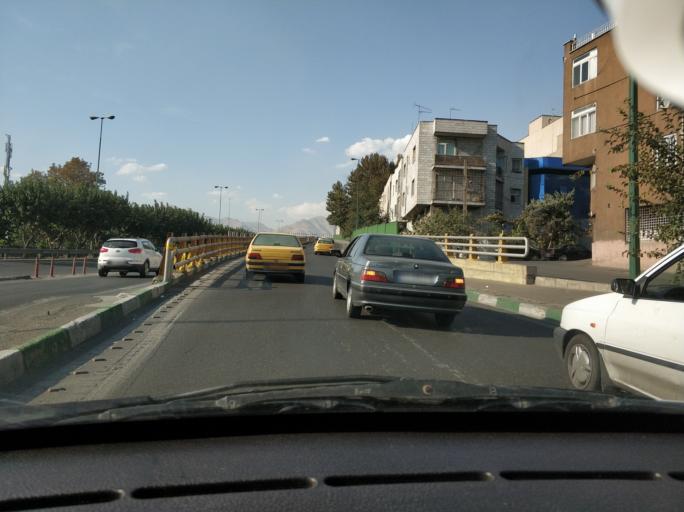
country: IR
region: Tehran
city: Tehran
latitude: 35.7353
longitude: 51.3713
